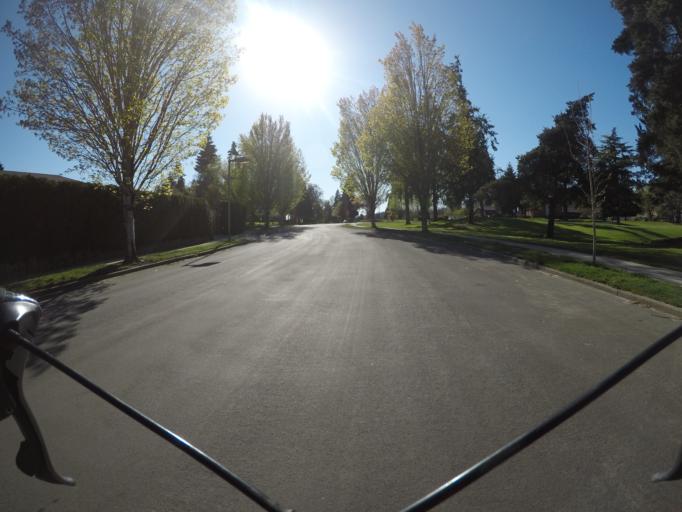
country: US
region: Oregon
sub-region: Washington County
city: Tigard
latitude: 45.4075
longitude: -122.7765
